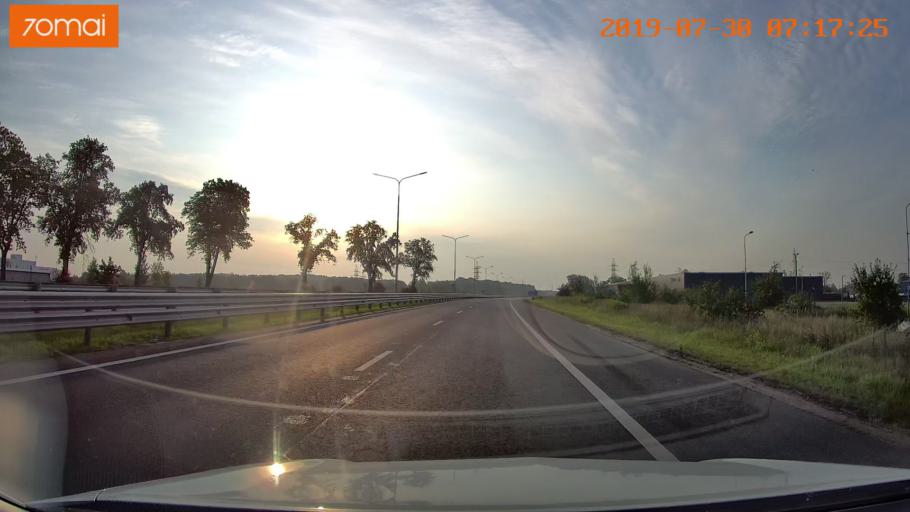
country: RU
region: Kaliningrad
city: Bol'shoe Isakovo
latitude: 54.7073
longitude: 20.6267
